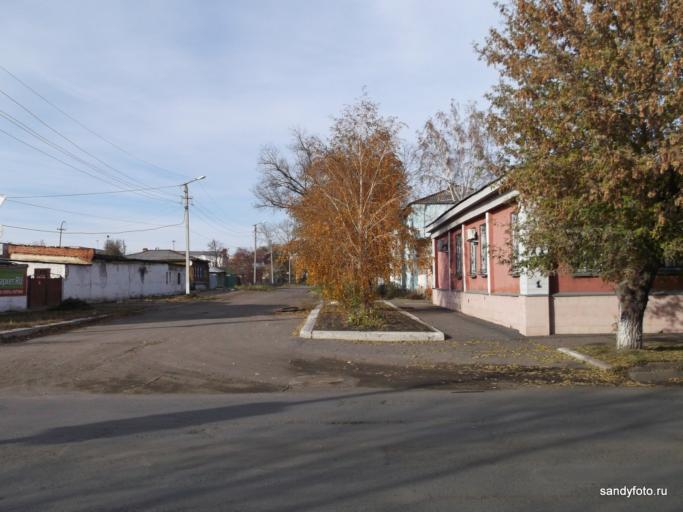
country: RU
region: Chelyabinsk
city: Troitsk
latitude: 54.0796
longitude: 61.5476
